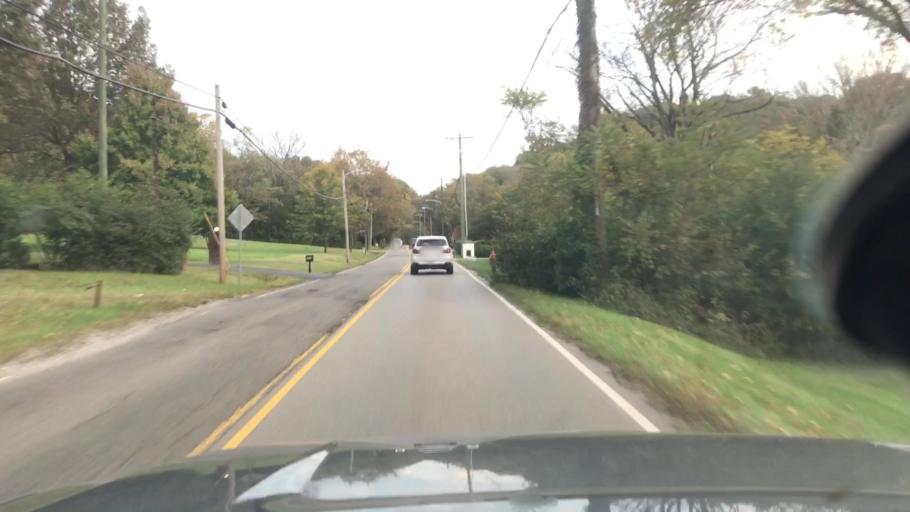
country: US
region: Tennessee
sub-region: Davidson County
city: Forest Hills
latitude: 36.0670
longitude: -86.8121
